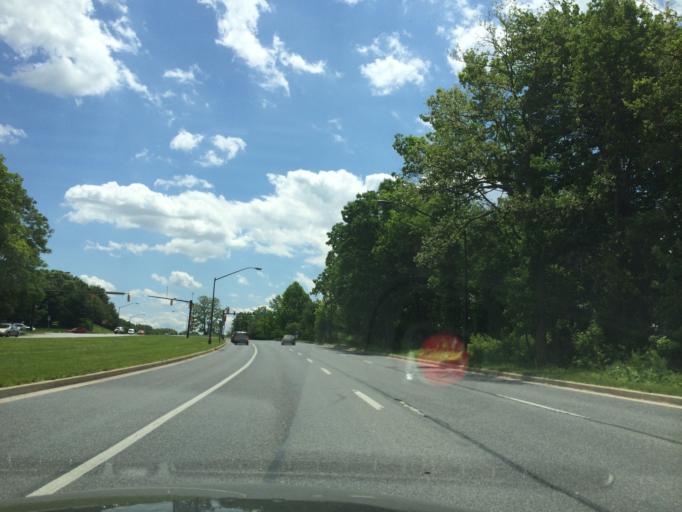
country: US
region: Maryland
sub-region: Howard County
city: Riverside
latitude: 39.1864
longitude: -76.8513
